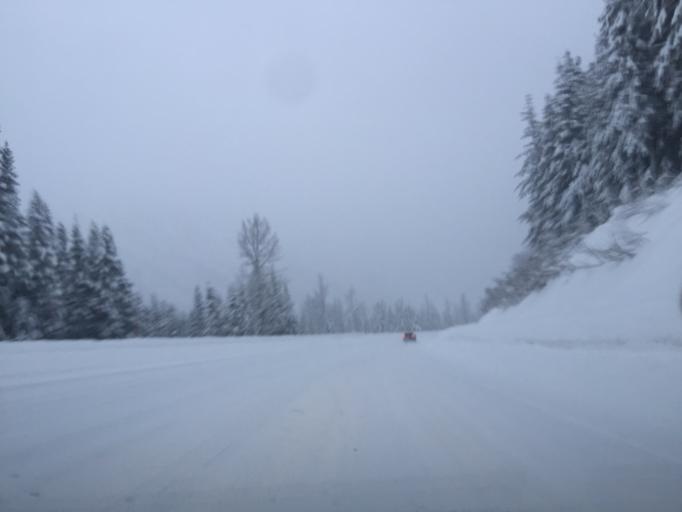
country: US
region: Washington
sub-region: Chelan County
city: Leavenworth
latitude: 47.7693
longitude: -121.0776
